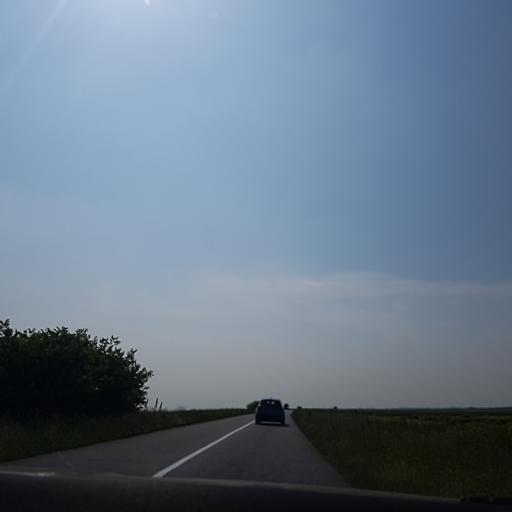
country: RS
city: Jarkovac
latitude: 45.3114
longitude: 20.7512
